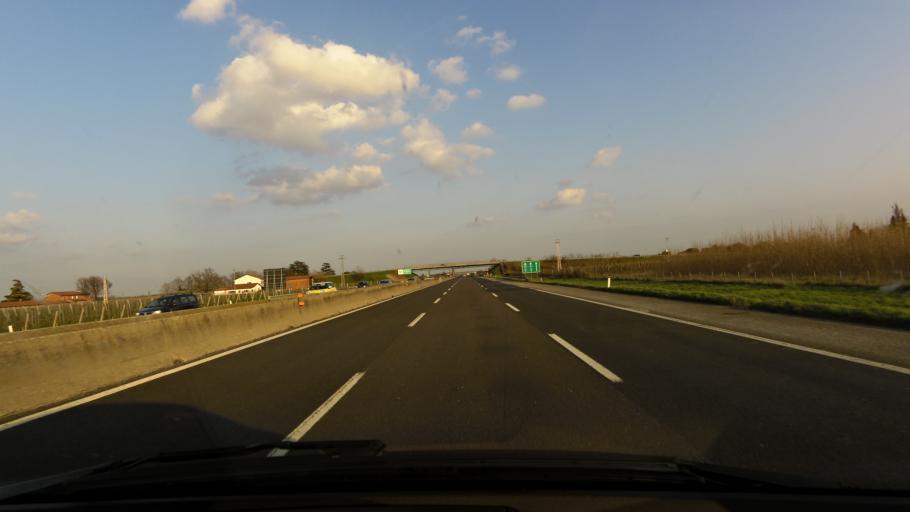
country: IT
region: Emilia-Romagna
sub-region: Provincia di Bologna
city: Imola
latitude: 44.3771
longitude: 11.7519
